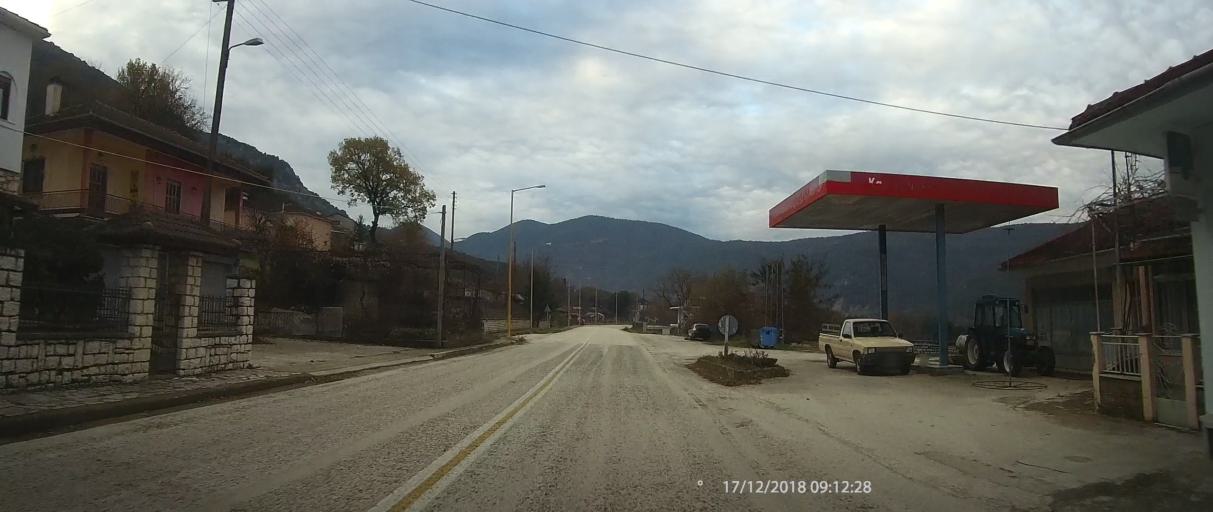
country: GR
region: Epirus
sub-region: Nomos Ioanninon
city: Kalpaki
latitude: 39.9809
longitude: 20.6660
